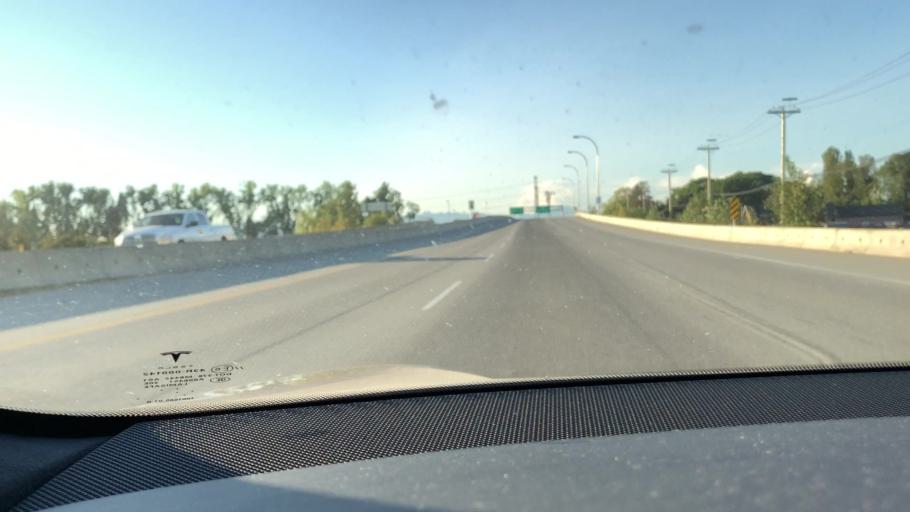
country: CA
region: British Columbia
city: Ladner
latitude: 49.0871
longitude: -123.0244
